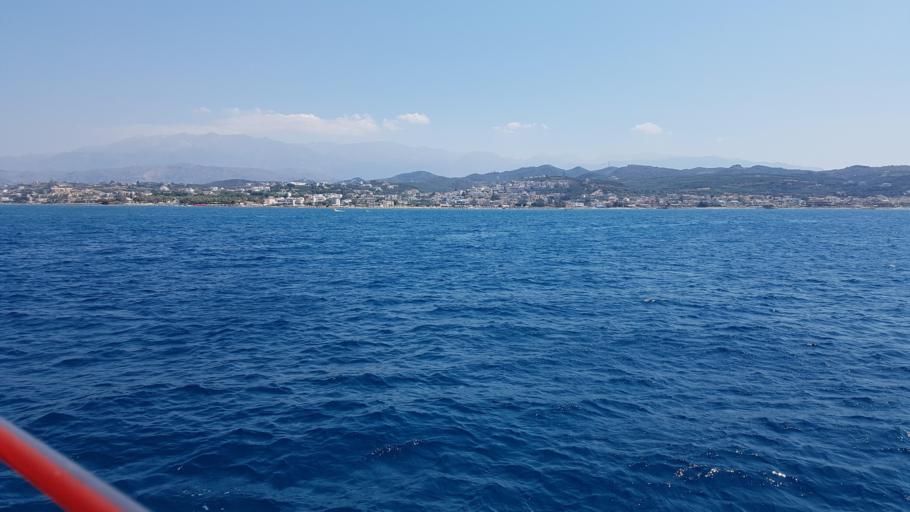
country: GR
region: Crete
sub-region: Nomos Chanias
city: Agia Marina
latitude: 35.5303
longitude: 23.9252
